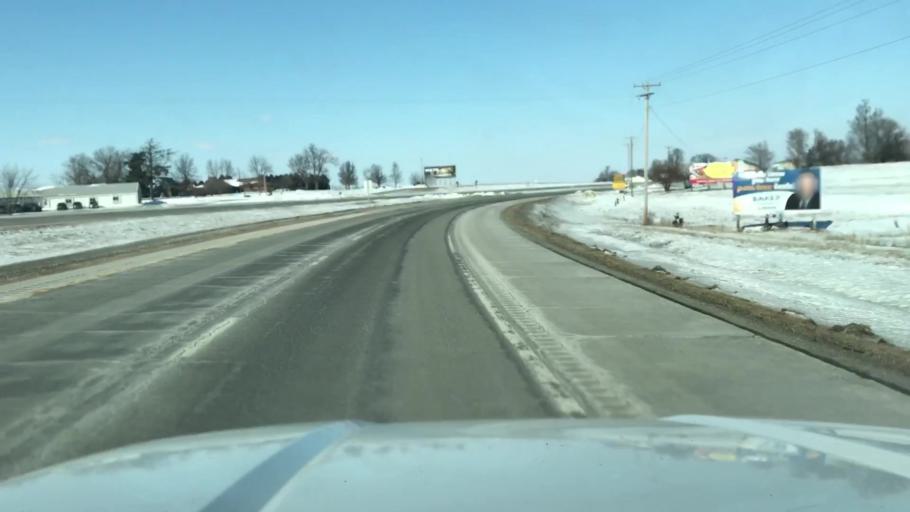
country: US
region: Missouri
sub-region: Nodaway County
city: Maryville
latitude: 40.2770
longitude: -94.8736
